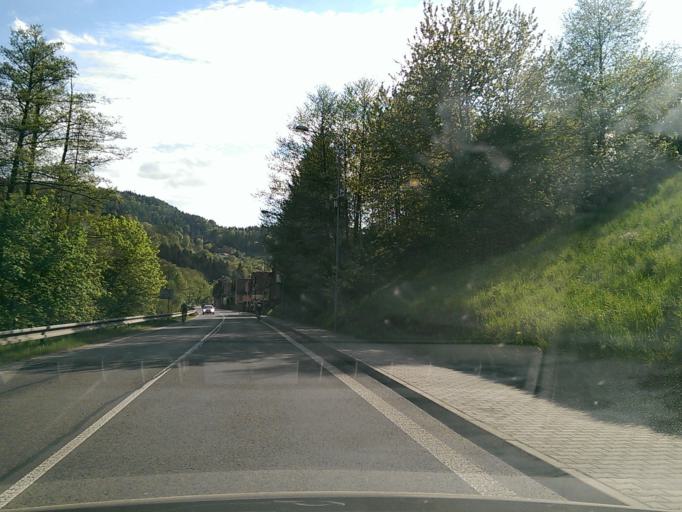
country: CZ
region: Liberecky
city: Mala Skala
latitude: 50.6489
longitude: 15.2099
